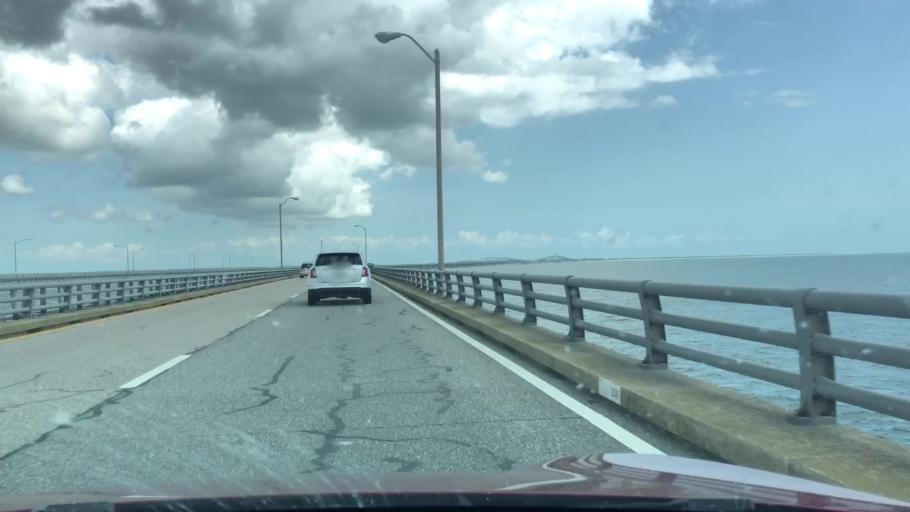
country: US
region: Virginia
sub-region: Northampton County
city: Cape Charles
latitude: 37.0752
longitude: -76.0207
